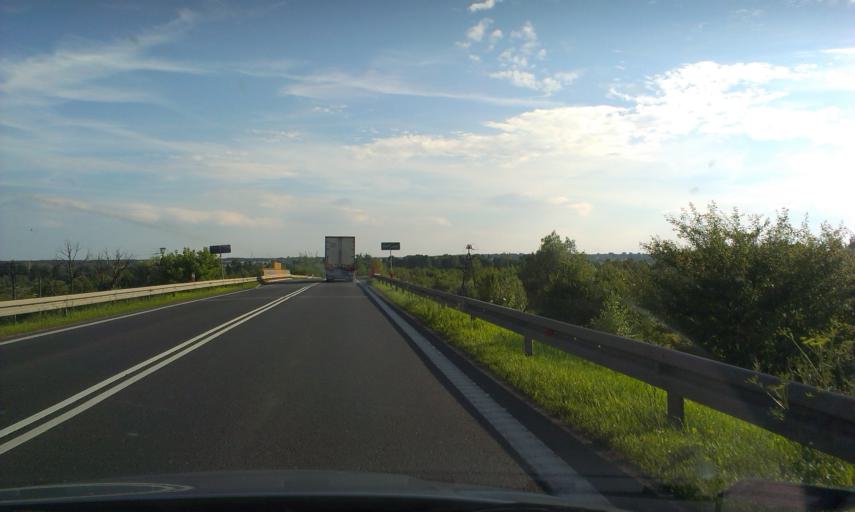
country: PL
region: Kujawsko-Pomorskie
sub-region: Powiat bydgoski
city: Biale Blota
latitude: 53.1532
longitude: 17.8865
